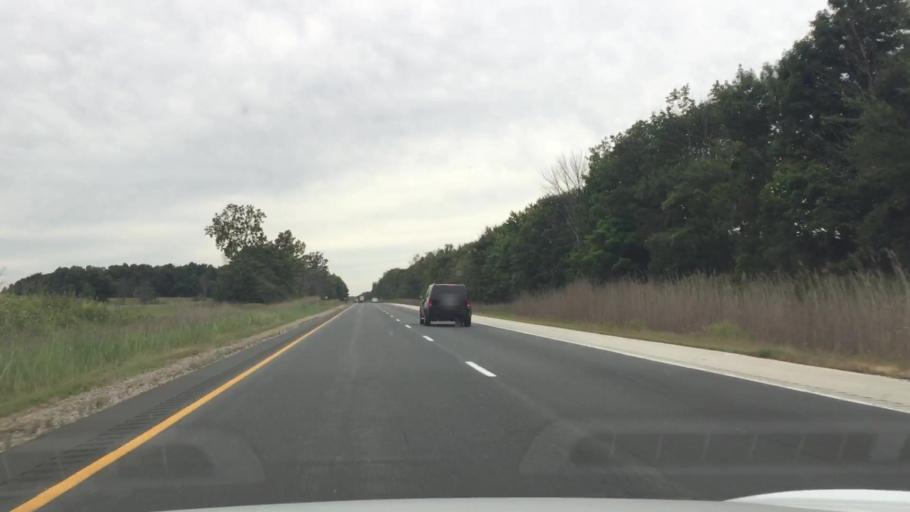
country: CA
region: Ontario
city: Camlachie
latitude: 42.9914
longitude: -82.0501
